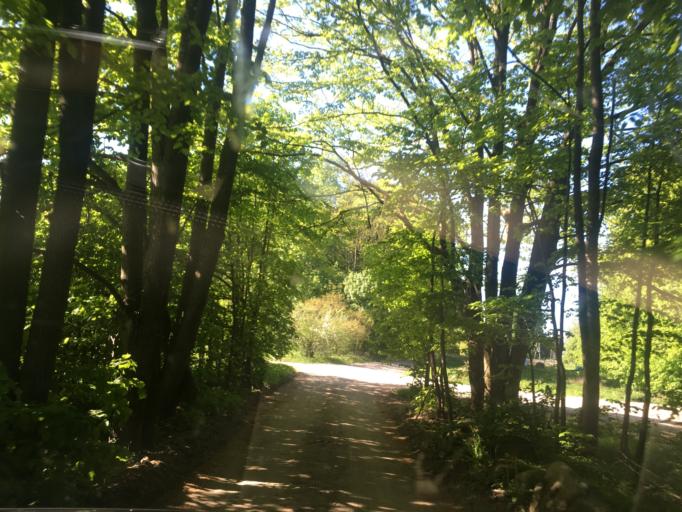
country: PL
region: Warmian-Masurian Voivodeship
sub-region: Powiat piski
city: Ruciane-Nida
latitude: 53.6543
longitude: 21.4841
